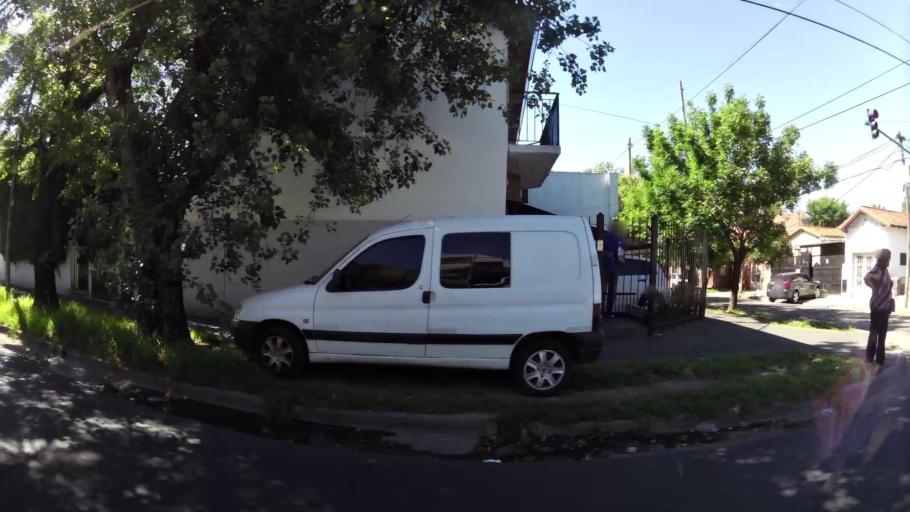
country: AR
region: Buenos Aires
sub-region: Partido de General San Martin
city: General San Martin
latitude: -34.5345
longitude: -58.5258
